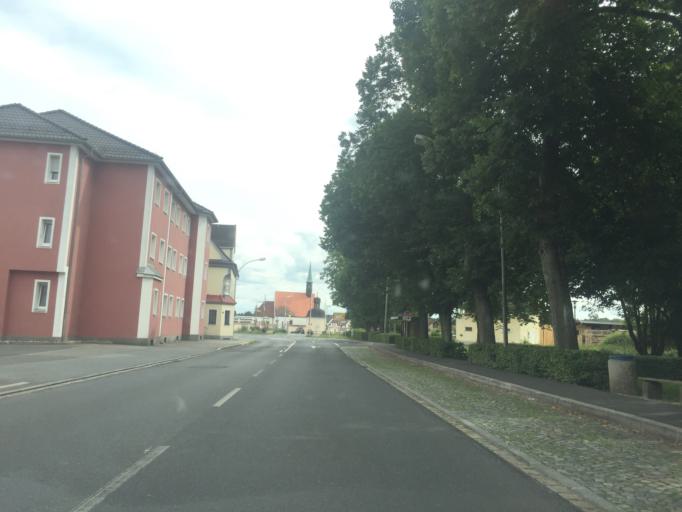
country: DE
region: Bavaria
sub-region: Upper Palatinate
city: Pressath
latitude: 49.7664
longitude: 11.9361
